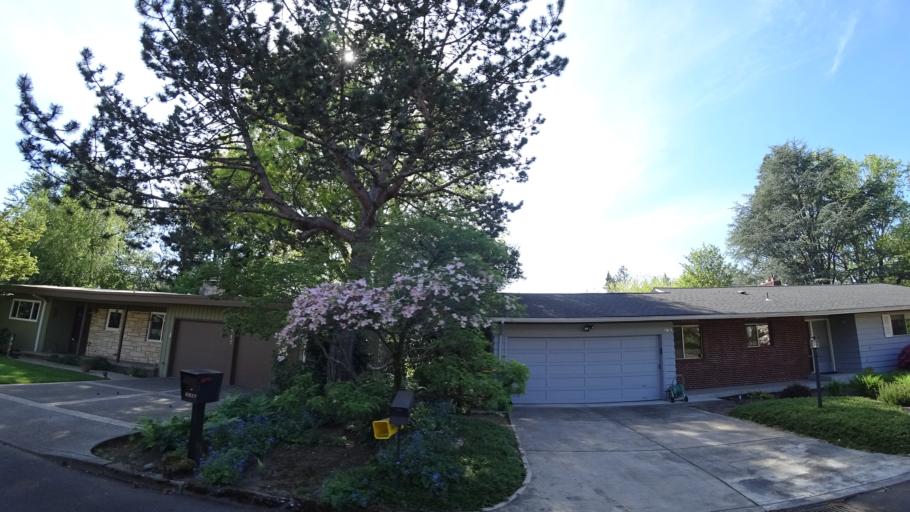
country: US
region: Oregon
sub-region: Washington County
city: Raleigh Hills
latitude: 45.4912
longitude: -122.7474
